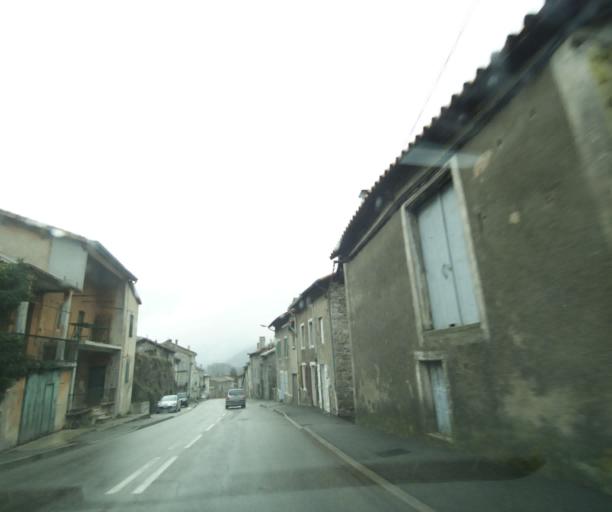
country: FR
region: Rhone-Alpes
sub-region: Departement de l'Ardeche
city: Thueyts
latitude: 44.6673
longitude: 4.1070
